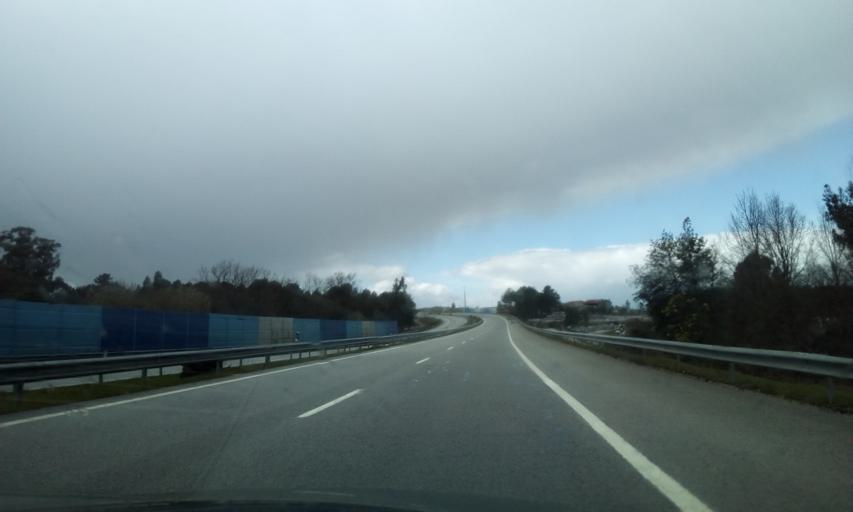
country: PT
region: Viseu
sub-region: Mangualde
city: Mangualde
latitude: 40.6138
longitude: -7.7144
